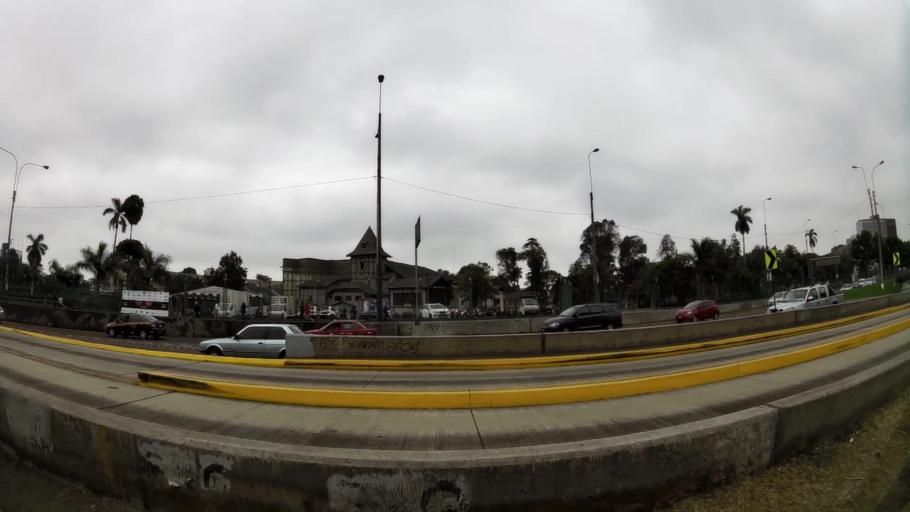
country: PE
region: Lima
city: Lima
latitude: -12.0615
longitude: -77.0347
